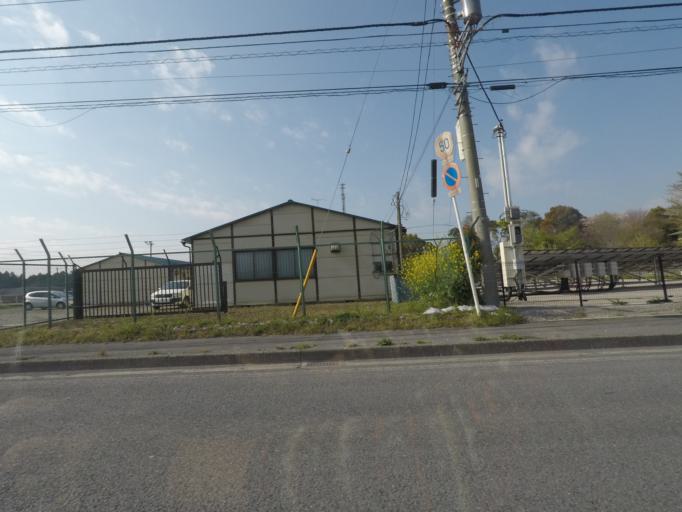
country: JP
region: Chiba
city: Narita
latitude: 35.8006
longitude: 140.3627
